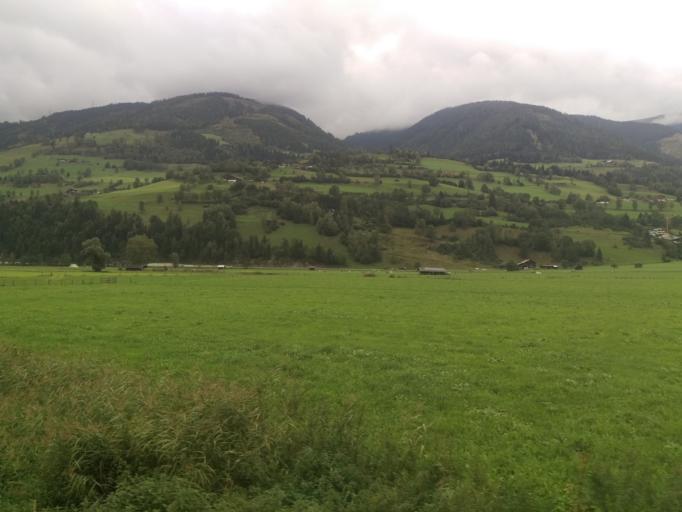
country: AT
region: Salzburg
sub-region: Politischer Bezirk Zell am See
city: Niedernsill
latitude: 47.2797
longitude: 12.6179
